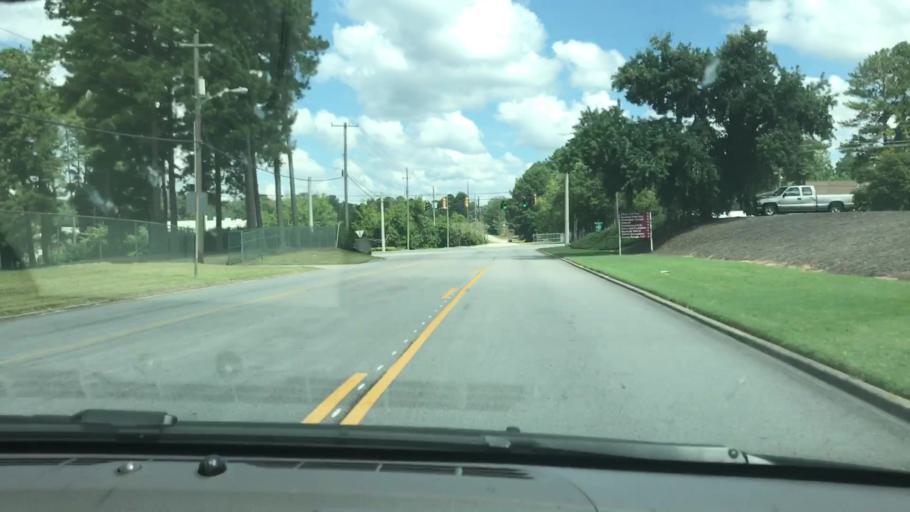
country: US
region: Georgia
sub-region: Troup County
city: La Grange
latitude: 33.0119
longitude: -85.0576
